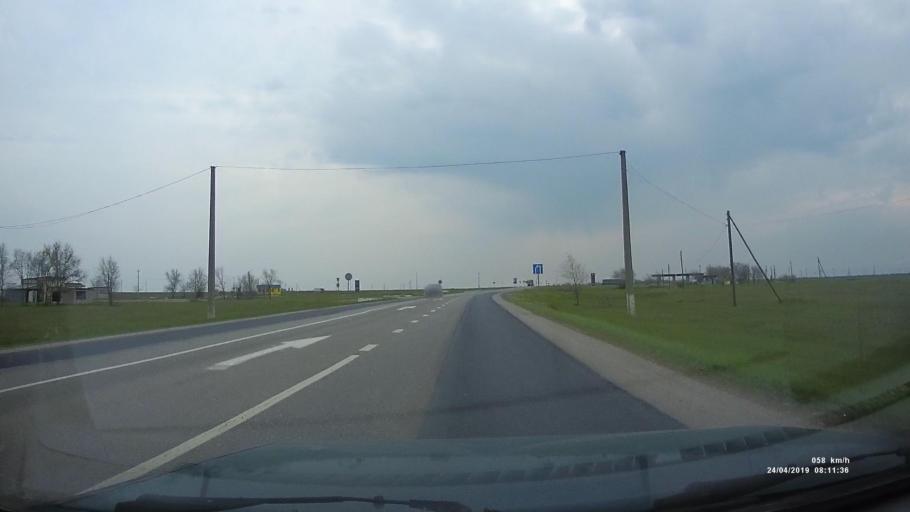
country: RU
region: Kalmykiya
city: Priyutnoye
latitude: 46.1026
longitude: 43.5302
